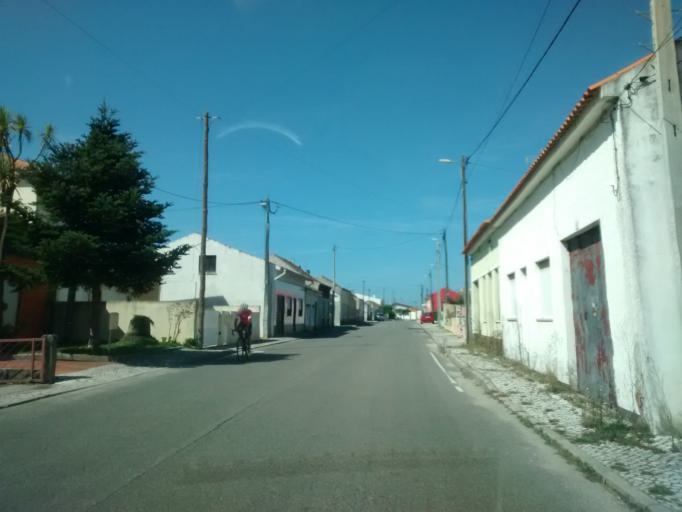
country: PT
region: Coimbra
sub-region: Mira
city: Mira
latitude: 40.4356
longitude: -8.7230
